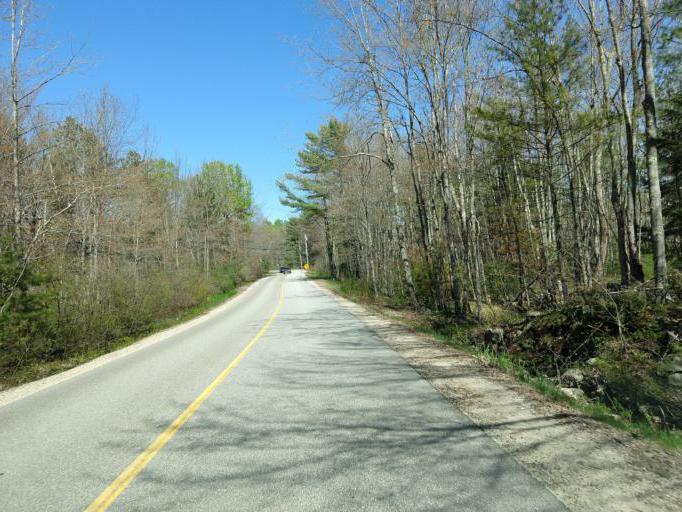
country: US
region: Maine
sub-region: York County
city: Arundel
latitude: 43.3915
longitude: -70.4561
